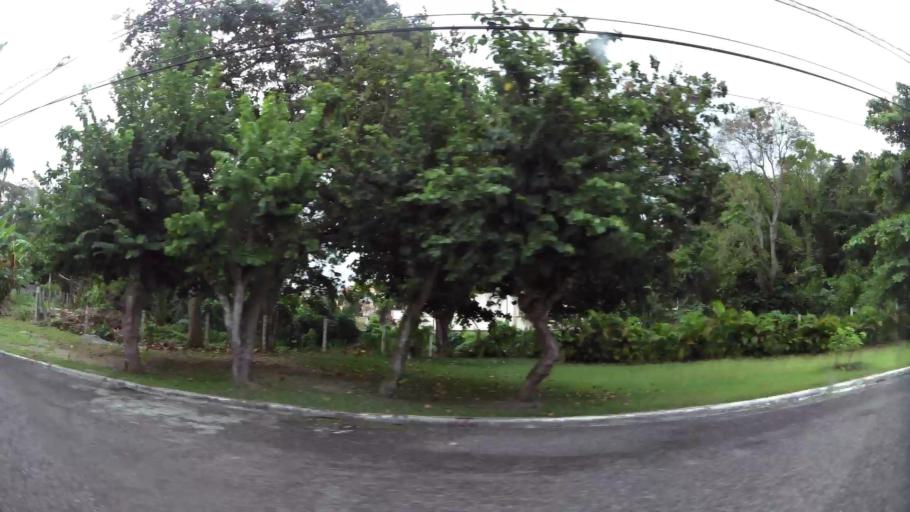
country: DO
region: Nacional
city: La Agustina
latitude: 18.5073
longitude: -69.9537
